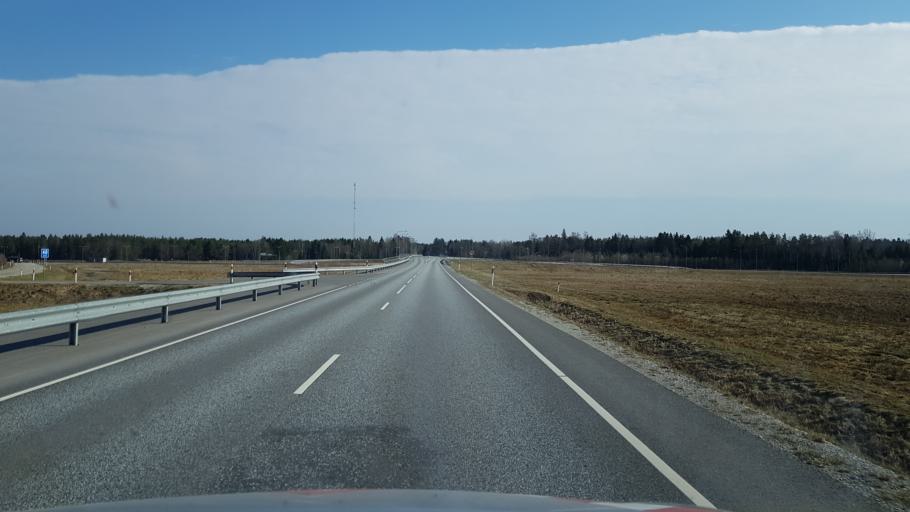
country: EE
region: Laeaene-Virumaa
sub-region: Kadrina vald
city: Kadrina
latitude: 59.4665
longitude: 25.9993
